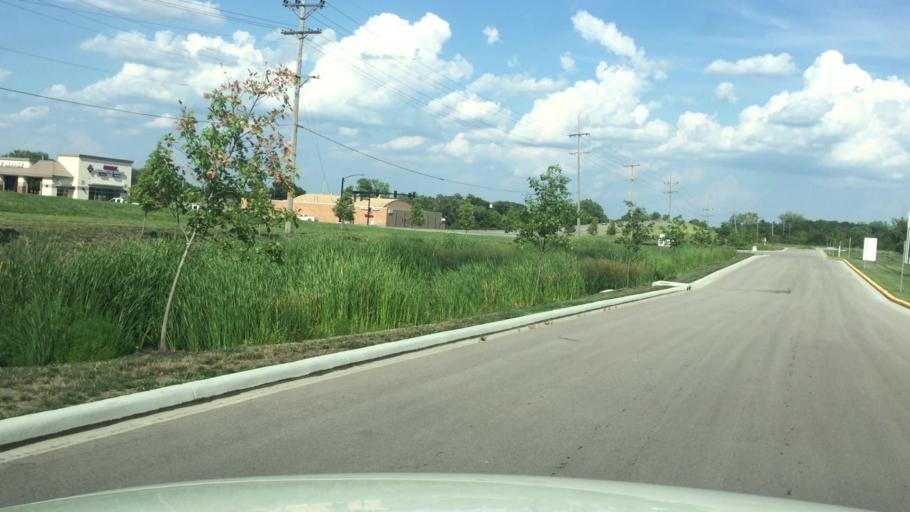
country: US
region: Kansas
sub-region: Johnson County
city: Olathe
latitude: 38.8671
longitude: -94.8314
